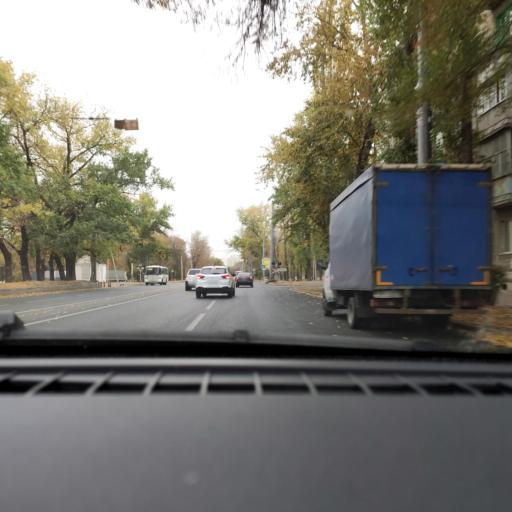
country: RU
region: Voronezj
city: Maslovka
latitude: 51.6104
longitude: 39.2454
